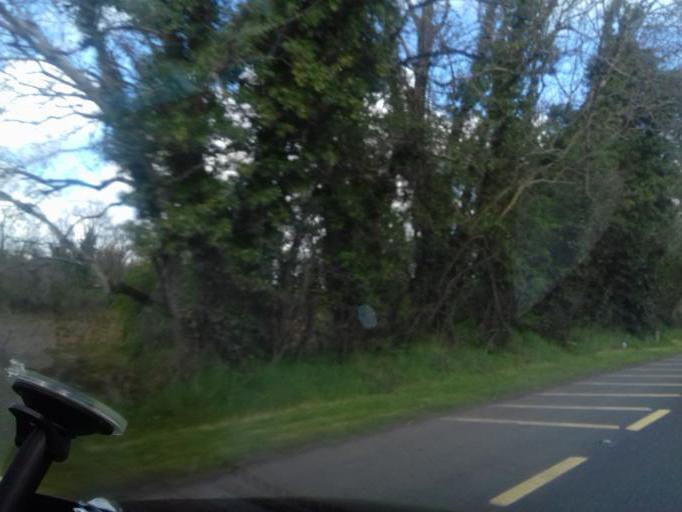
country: IE
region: Ulster
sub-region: An Cabhan
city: Ballyjamesduff
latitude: 53.9615
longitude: -7.2289
